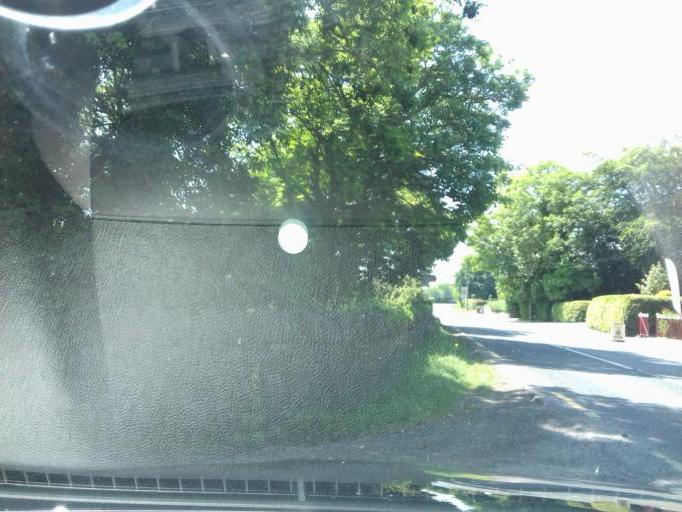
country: IE
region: Leinster
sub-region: An Mhi
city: Slane
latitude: 53.7070
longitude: -6.5272
